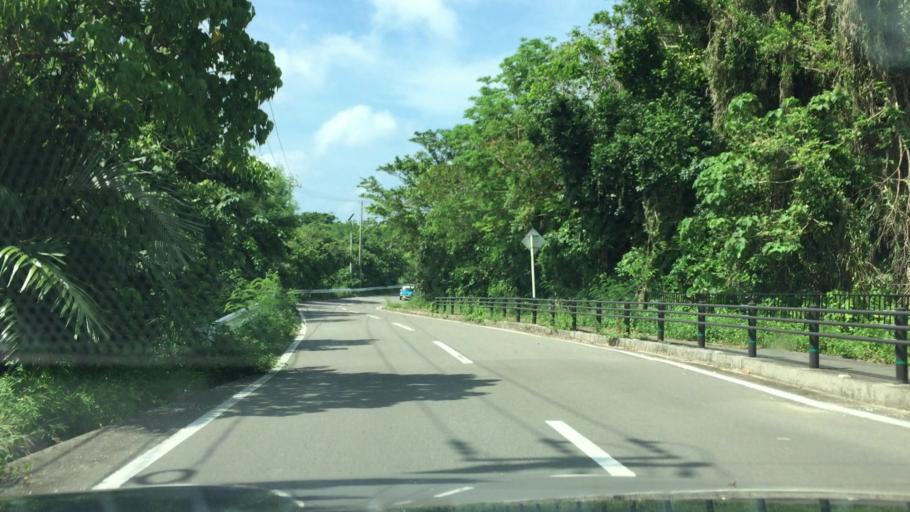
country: JP
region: Okinawa
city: Ishigaki
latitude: 24.4878
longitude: 124.2314
